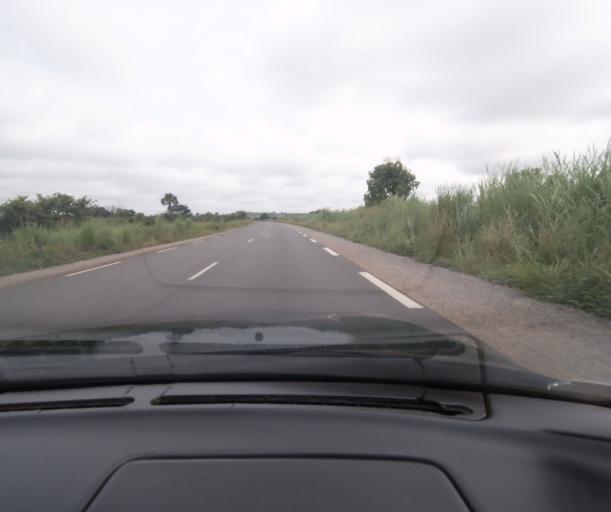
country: CM
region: Centre
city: Saa
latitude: 4.3881
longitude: 11.2551
